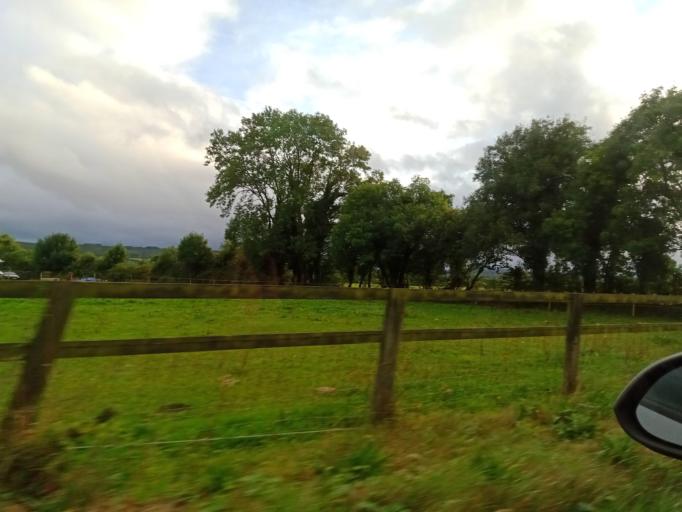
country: IE
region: Leinster
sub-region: Uibh Fhaili
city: Tullamore
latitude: 53.1441
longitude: -7.4664
